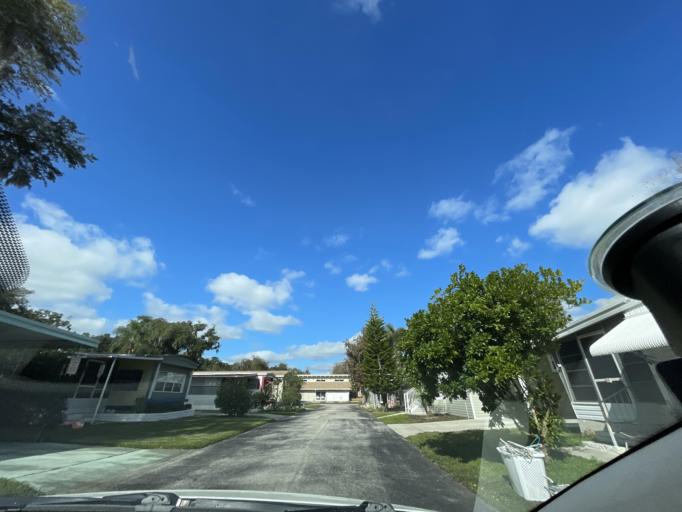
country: US
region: Florida
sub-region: Volusia County
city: South Daytona
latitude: 29.1691
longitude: -81.0272
